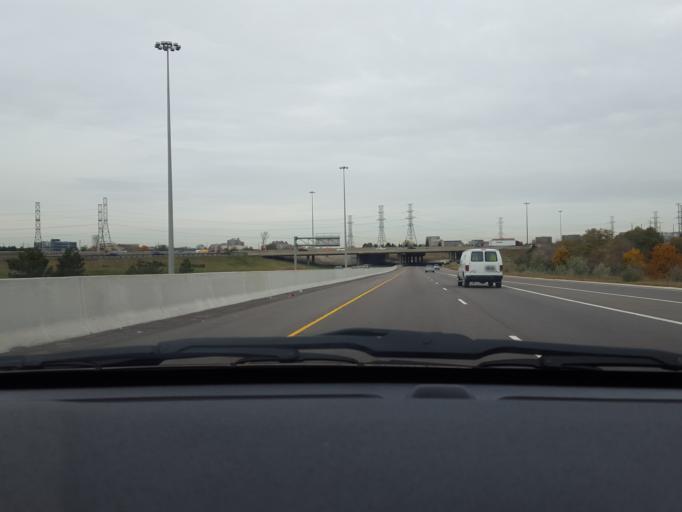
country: CA
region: Ontario
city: Etobicoke
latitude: 43.6744
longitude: -79.5746
